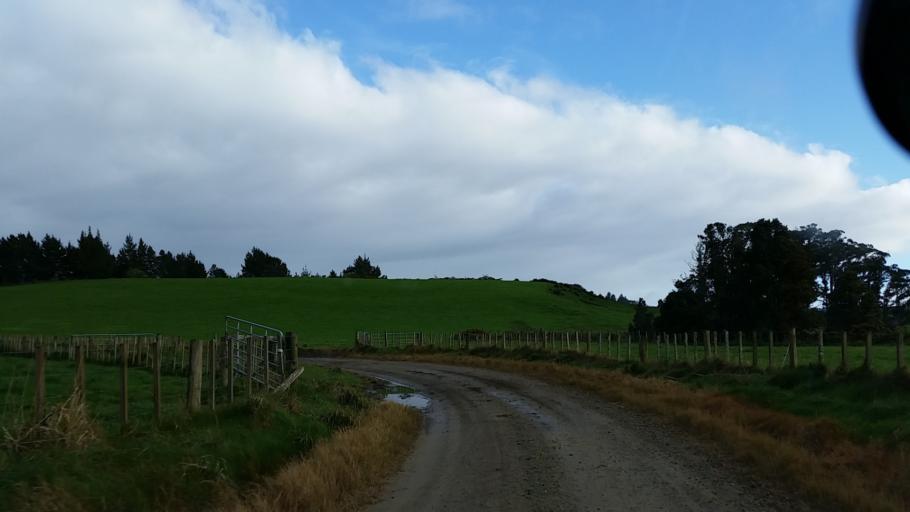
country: NZ
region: Taranaki
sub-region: South Taranaki District
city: Patea
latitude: -39.7240
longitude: 174.7200
